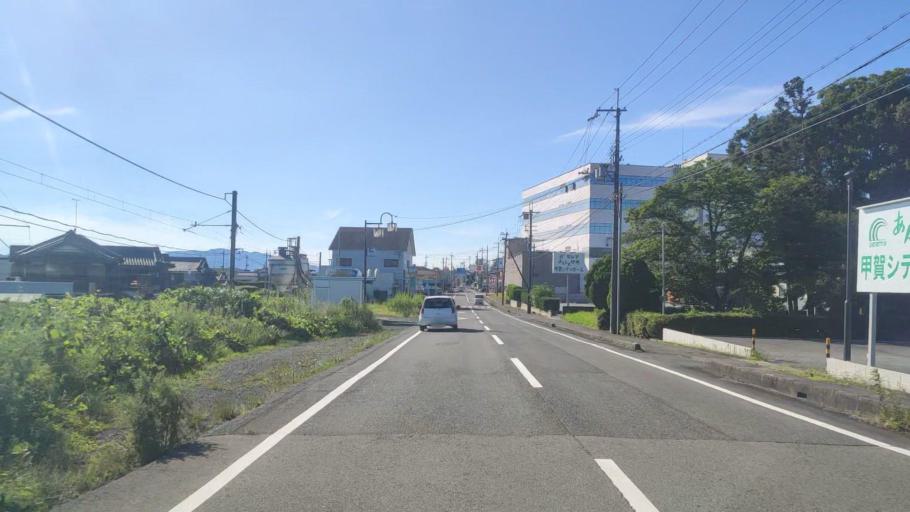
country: JP
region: Shiga Prefecture
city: Minakuchicho-matoba
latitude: 34.8987
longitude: 136.2170
